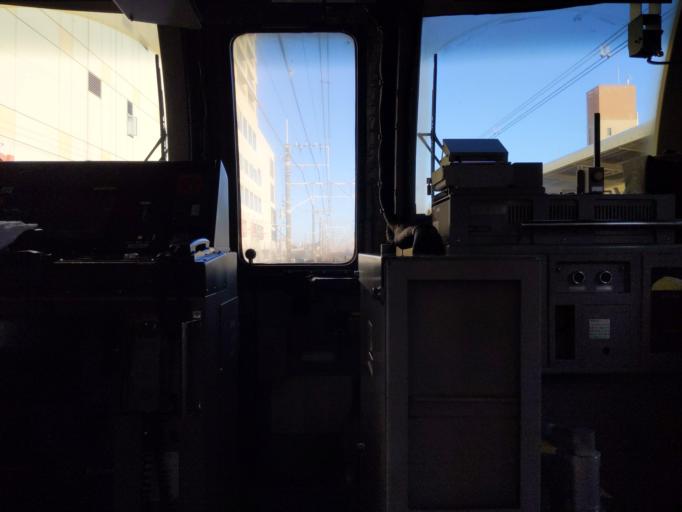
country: JP
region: Chiba
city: Funabashi
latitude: 35.7143
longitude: 139.9433
